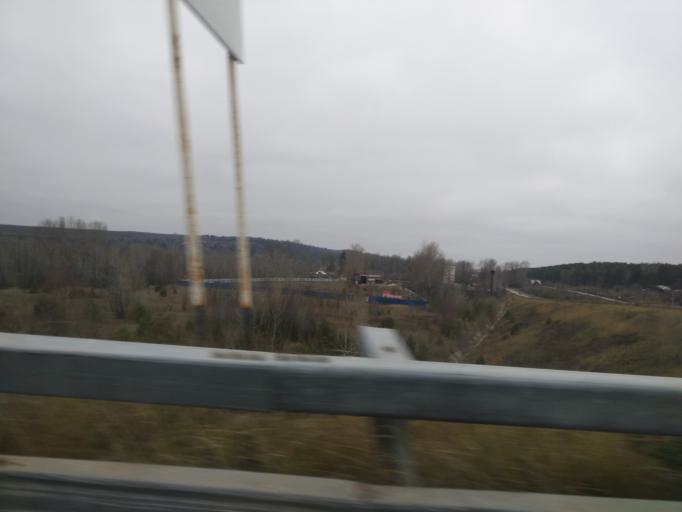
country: RU
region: Kirov
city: Sosnovka
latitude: 56.2497
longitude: 51.2198
